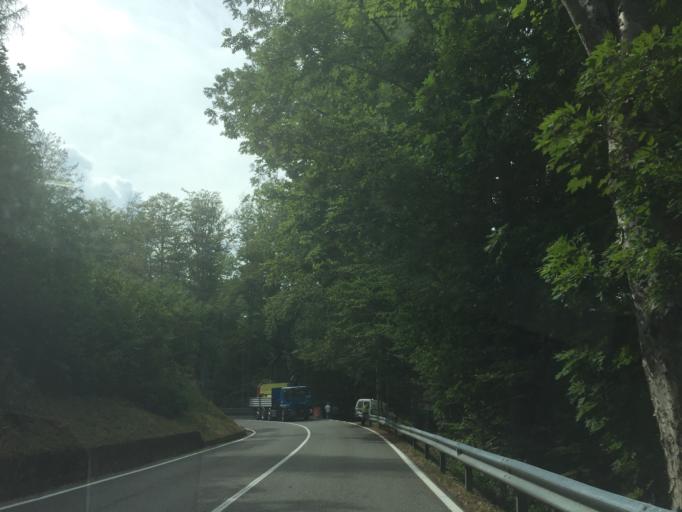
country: IT
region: Tuscany
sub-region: Provincia di Pistoia
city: Abetone
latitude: 44.1250
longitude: 10.7017
